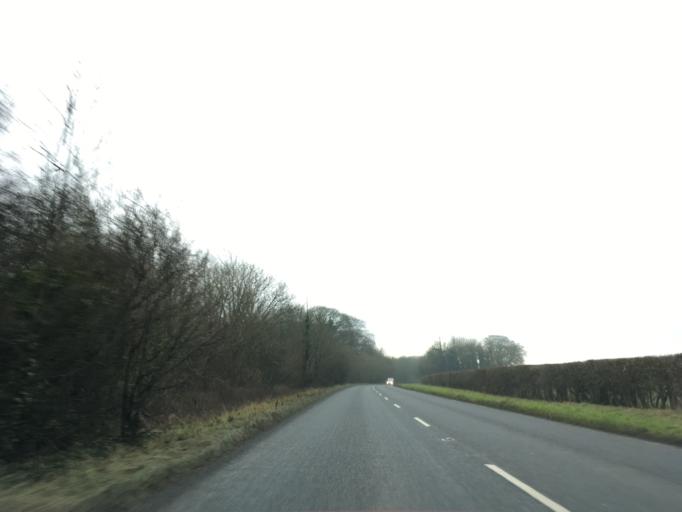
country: GB
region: England
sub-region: Gloucestershire
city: Nailsworth
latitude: 51.6327
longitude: -2.2535
